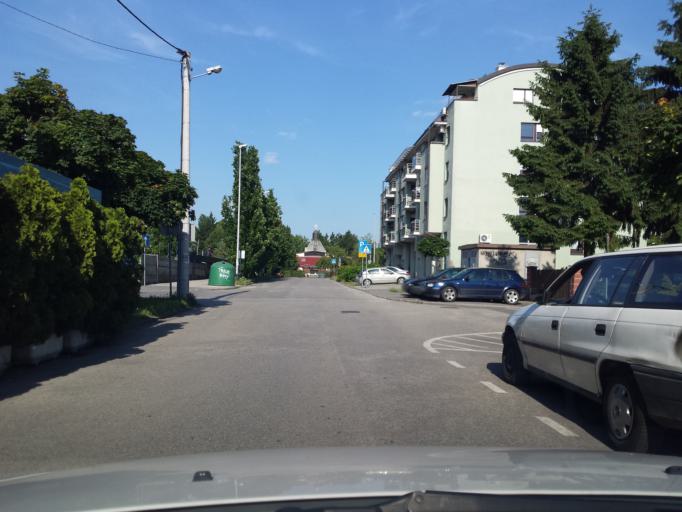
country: HR
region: Grad Zagreb
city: Novi Zagreb
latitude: 45.7972
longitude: 15.9832
